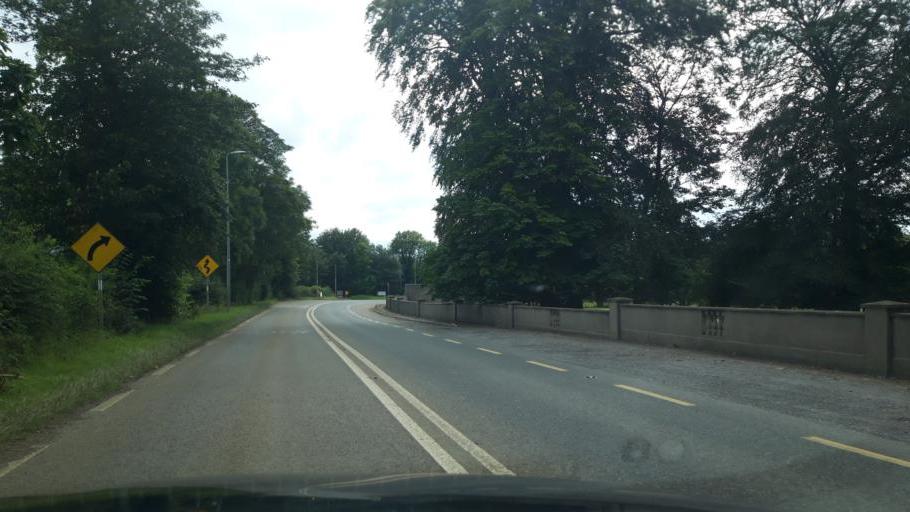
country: IE
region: Leinster
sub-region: Kilkenny
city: Castlecomer
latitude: 52.8434
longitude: -7.1293
